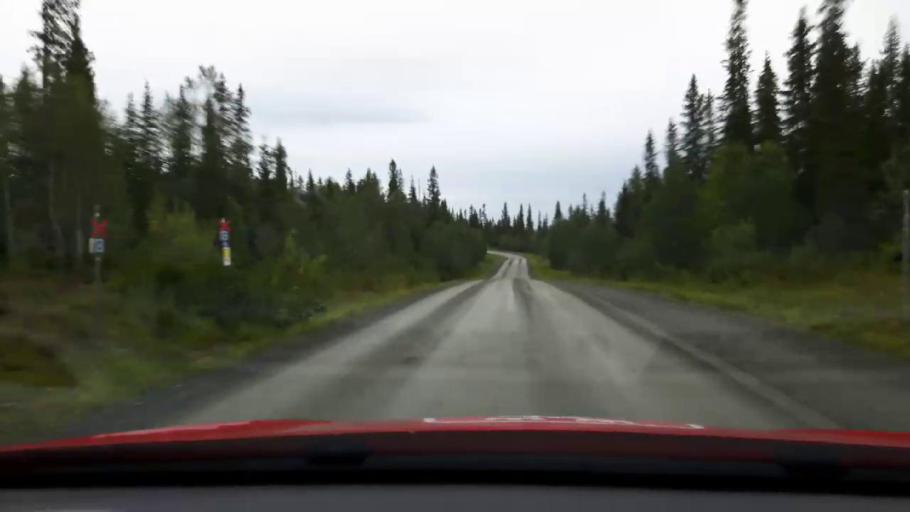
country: SE
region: Jaemtland
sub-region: Are Kommun
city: Are
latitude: 63.4013
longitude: 13.2028
